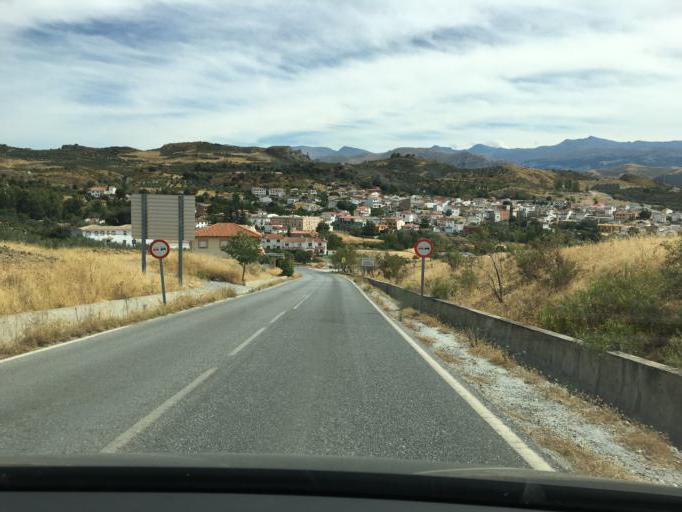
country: ES
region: Andalusia
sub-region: Provincia de Granada
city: Beas de Granada
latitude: 37.2230
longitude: -3.4861
